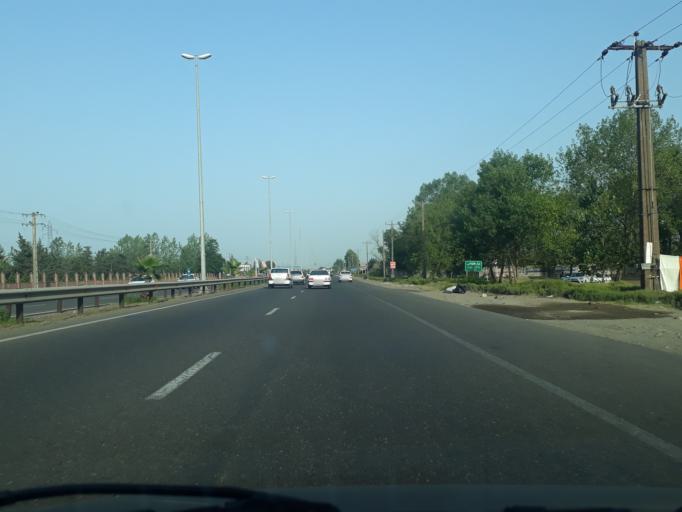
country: IR
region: Gilan
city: Bandar-e Anzali
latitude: 37.4605
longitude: 49.5746
